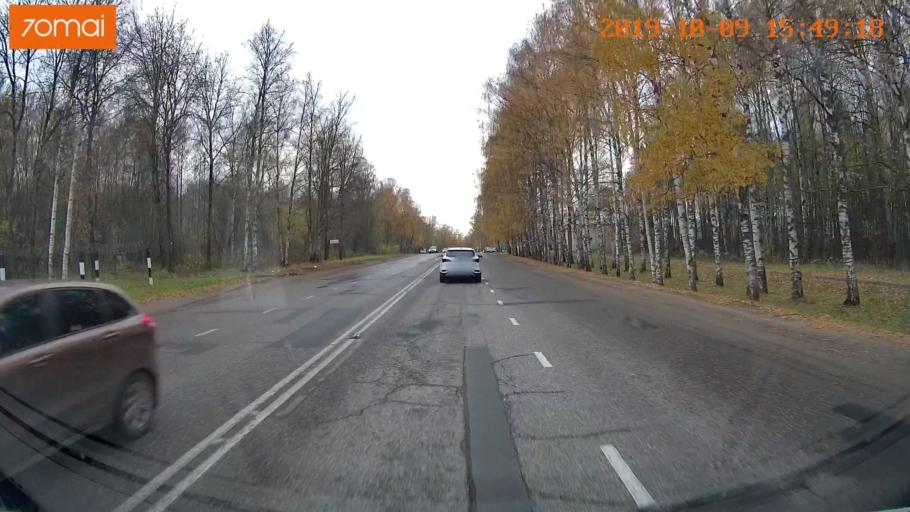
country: RU
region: Kostroma
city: Oktyabr'skiy
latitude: 57.8059
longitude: 41.0063
